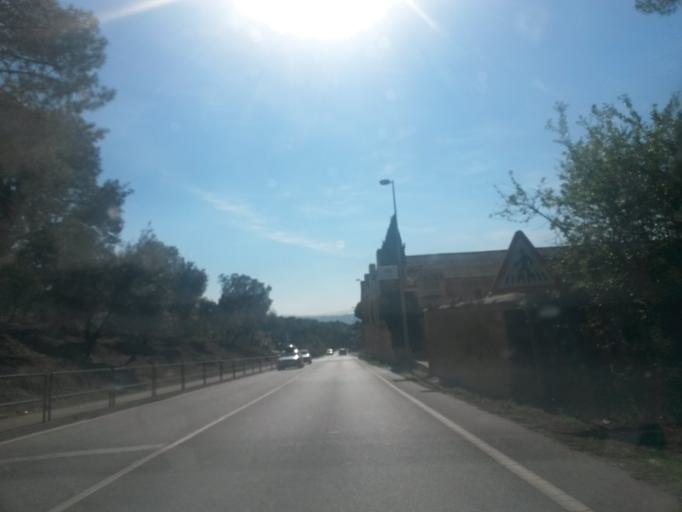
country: ES
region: Catalonia
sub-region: Provincia de Girona
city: Begur
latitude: 41.9533
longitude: 3.2001
